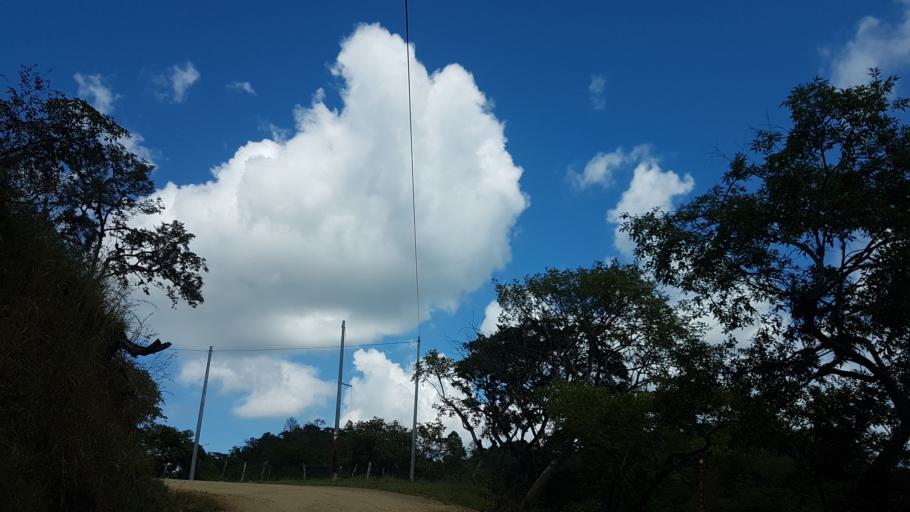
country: HN
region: El Paraiso
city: Oropoli
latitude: 13.7397
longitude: -86.7015
